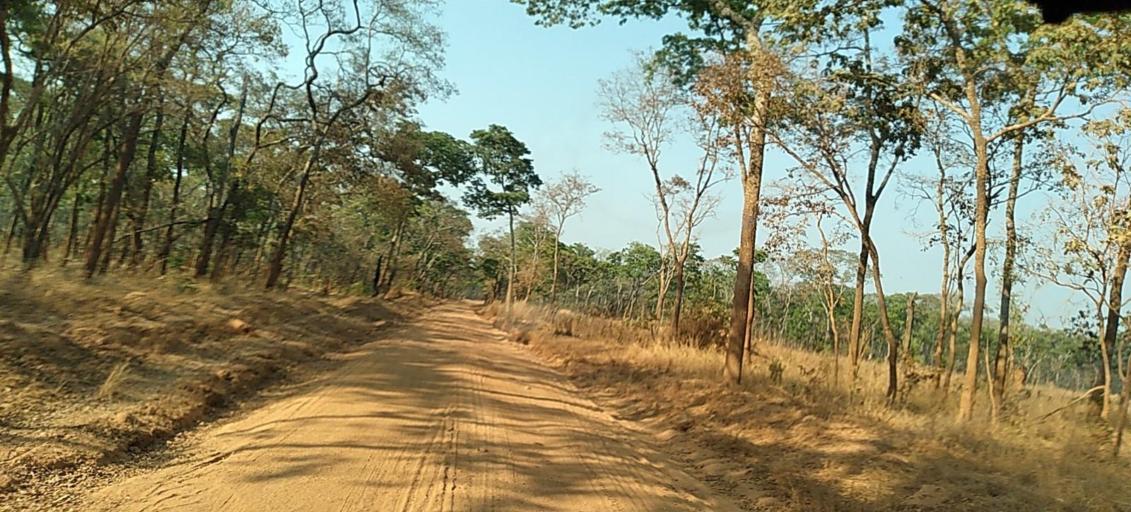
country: ZM
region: North-Western
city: Kasempa
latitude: -13.5759
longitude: 25.9914
